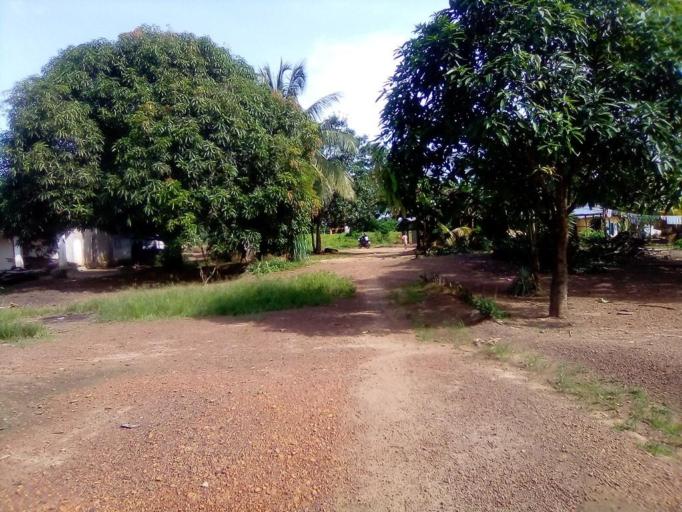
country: SL
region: Southern Province
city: Pujehun
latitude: 7.3636
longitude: -11.7265
